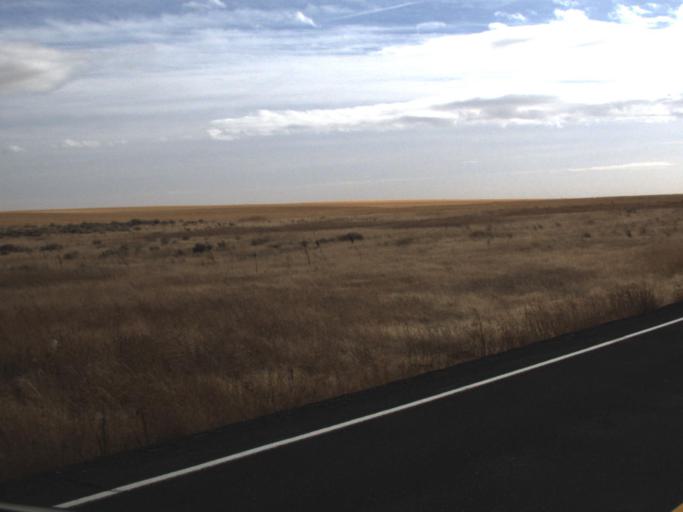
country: US
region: Washington
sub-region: Okanogan County
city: Coulee Dam
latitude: 47.7529
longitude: -118.7217
